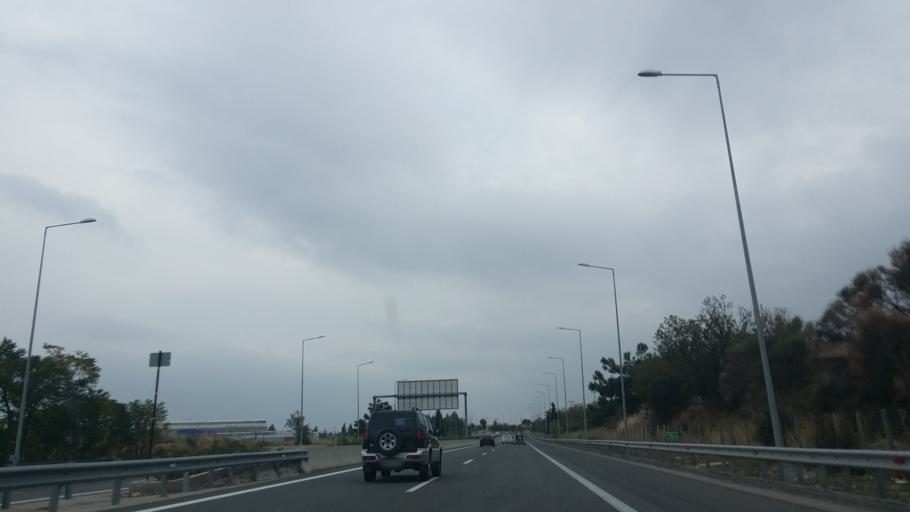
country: GR
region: Central Greece
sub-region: Nomos Voiotias
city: Arma
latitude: 38.3785
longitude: 23.5022
